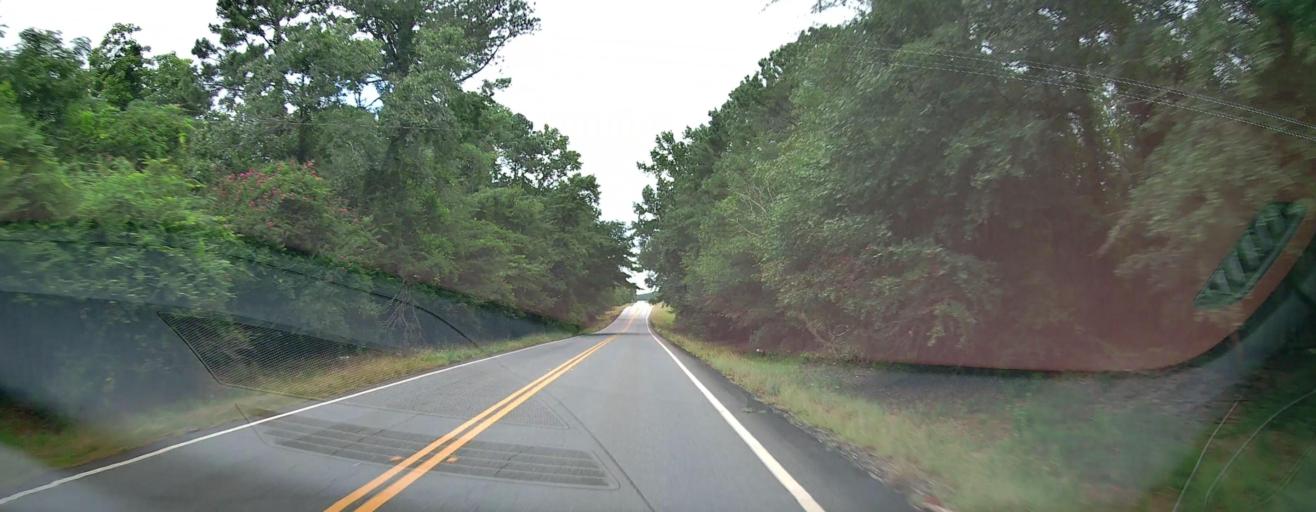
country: US
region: Georgia
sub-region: Marion County
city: Buena Vista
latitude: 32.2795
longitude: -84.4385
